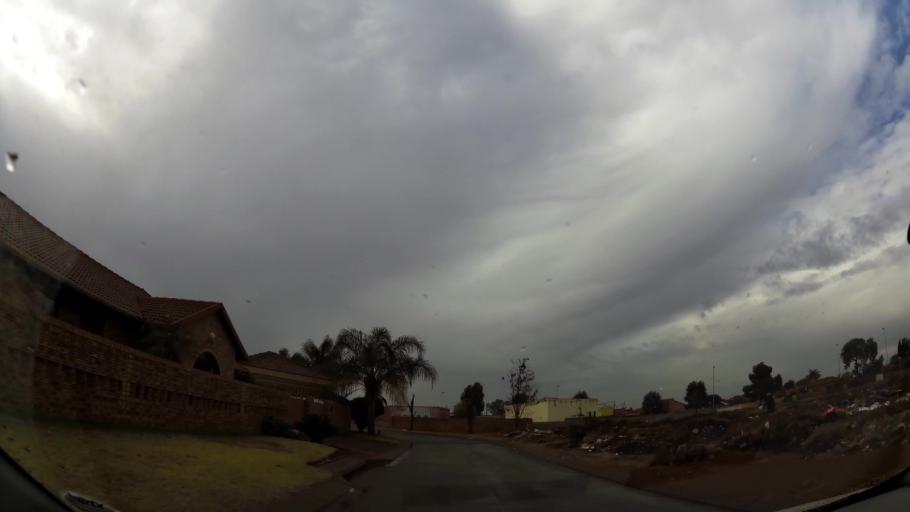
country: ZA
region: Gauteng
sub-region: Ekurhuleni Metropolitan Municipality
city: Germiston
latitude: -26.3280
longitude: 28.1912
